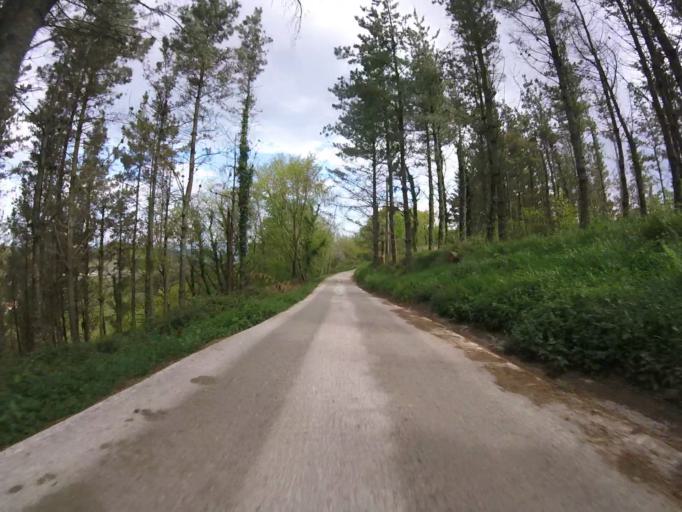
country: ES
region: Basque Country
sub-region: Provincia de Guipuzcoa
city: Zarautz
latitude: 43.2508
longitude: -2.1834
